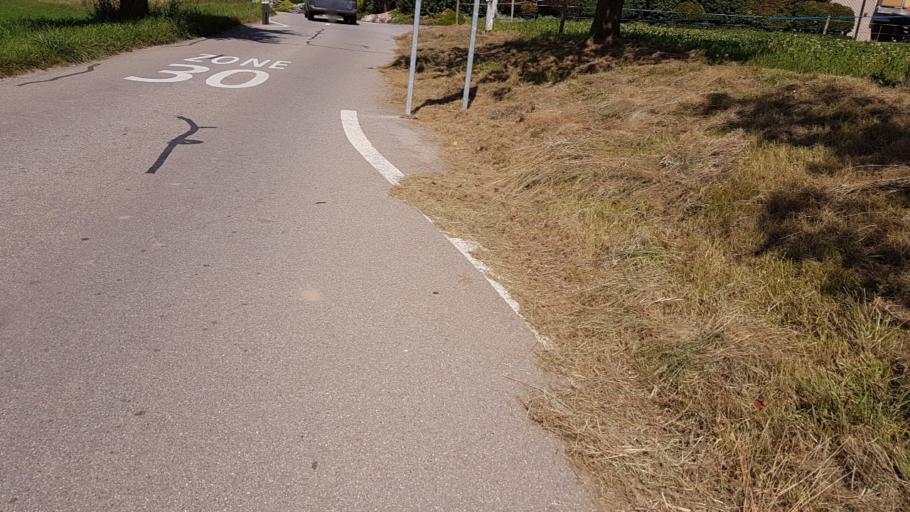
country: CH
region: Bern
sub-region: Bern-Mittelland District
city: Konolfingen
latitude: 46.8651
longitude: 7.6288
